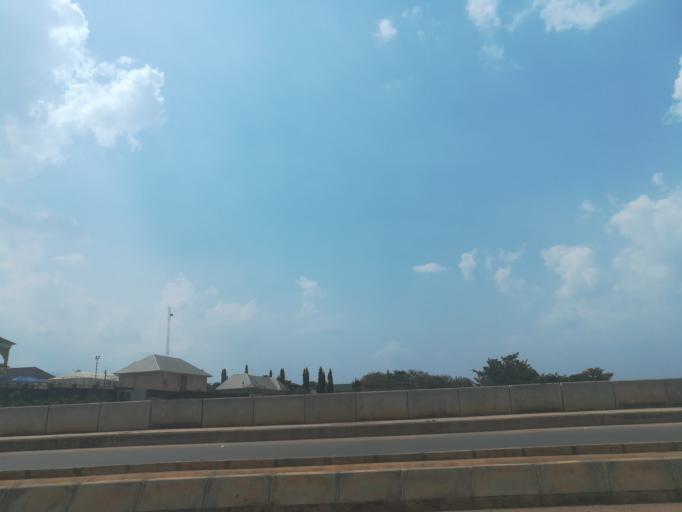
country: NG
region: Abuja Federal Capital Territory
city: Abuja
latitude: 9.0570
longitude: 7.4443
